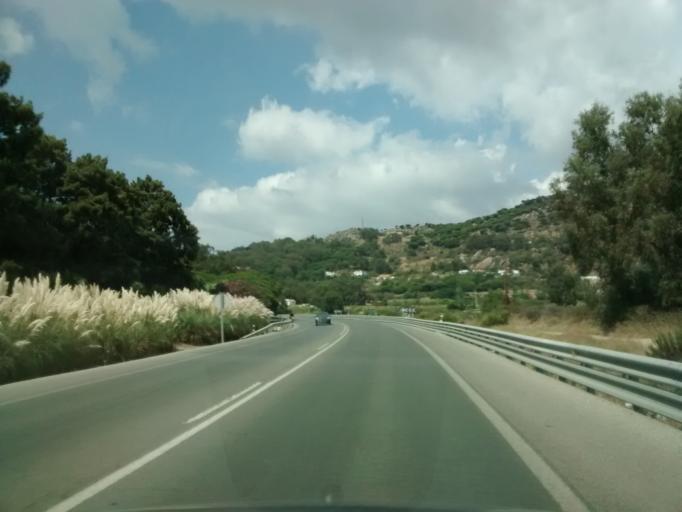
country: ES
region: Andalusia
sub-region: Provincia de Cadiz
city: Tarifa
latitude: 36.0555
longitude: -5.6507
